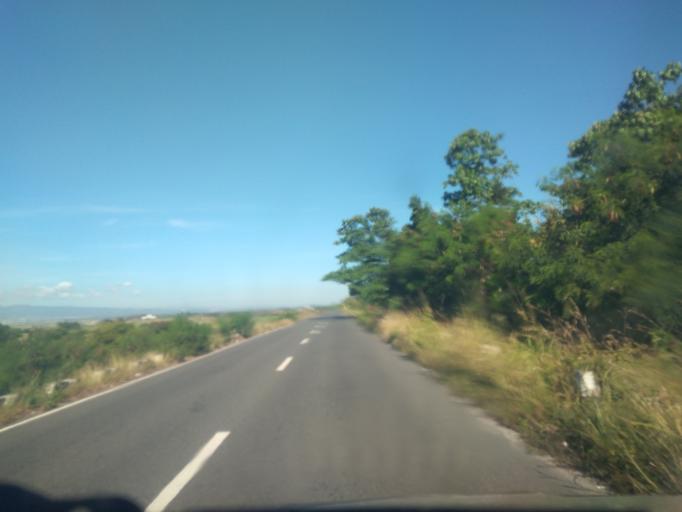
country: PH
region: Central Luzon
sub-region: Province of Pampanga
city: Bulaon
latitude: 15.0642
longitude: 120.6316
